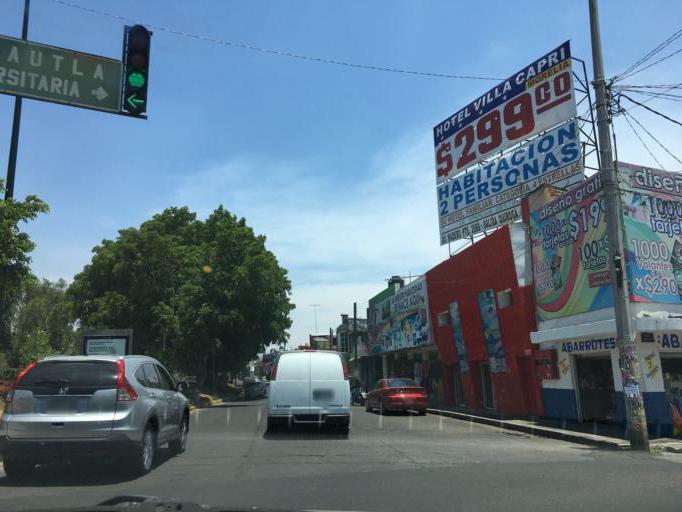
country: MX
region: Michoacan
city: Morelia
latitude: 19.6933
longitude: -101.2003
